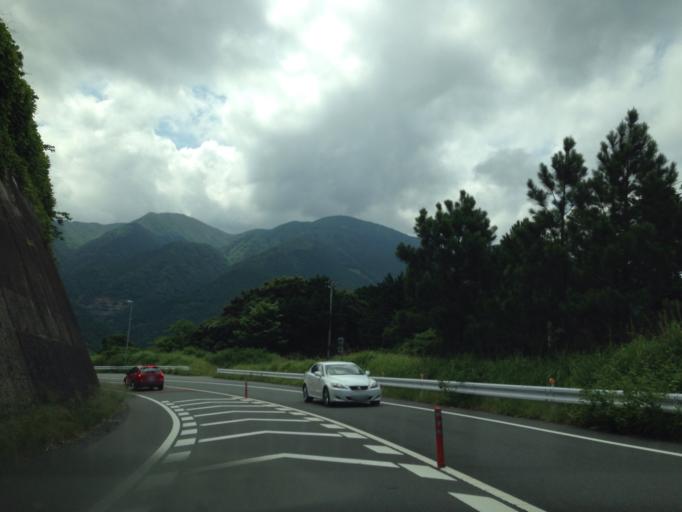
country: JP
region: Shizuoka
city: Heda
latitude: 34.9112
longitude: 138.8123
